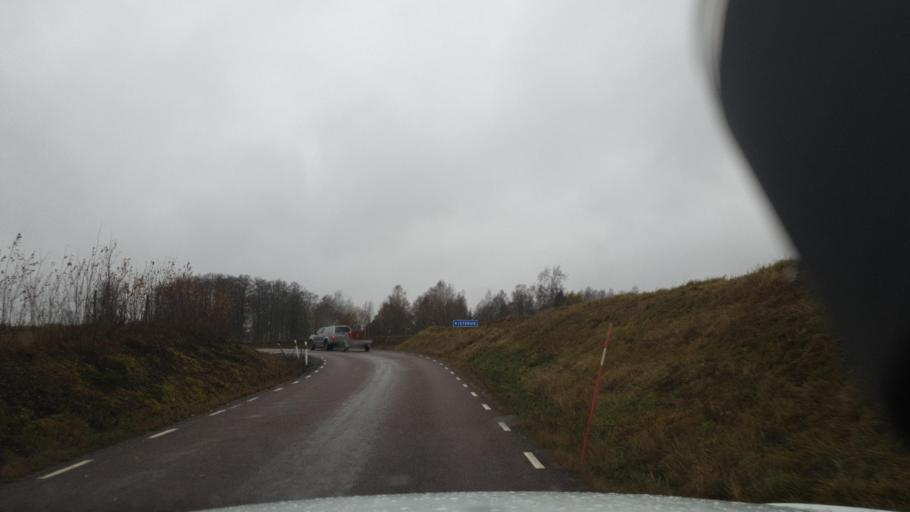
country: SE
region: Vaermland
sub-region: Sunne Kommun
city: Sunne
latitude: 59.7395
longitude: 13.1174
